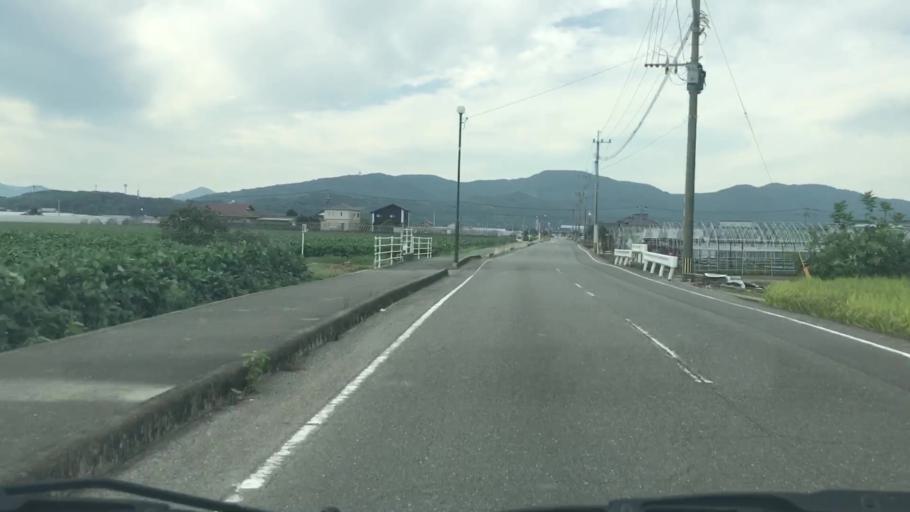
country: JP
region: Saga Prefecture
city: Kashima
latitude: 33.1452
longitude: 130.1383
